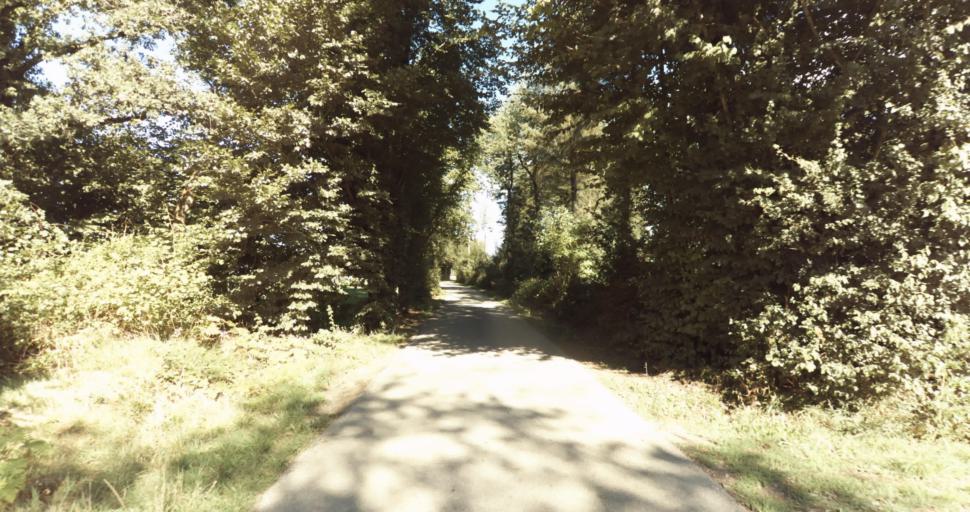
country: FR
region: Lower Normandy
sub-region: Departement de l'Orne
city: Gace
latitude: 48.7935
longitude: 0.2333
